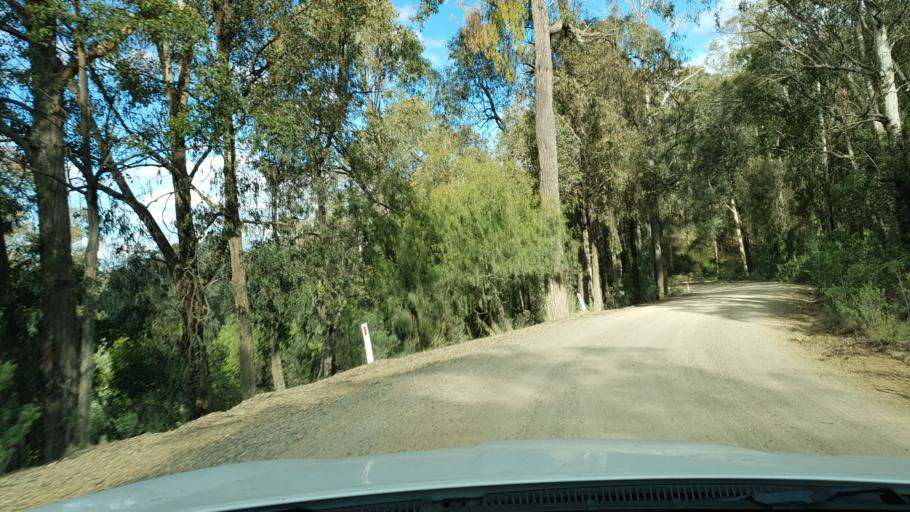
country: AU
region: Victoria
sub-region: East Gippsland
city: Bairnsdale
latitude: -37.6940
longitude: 147.5703
